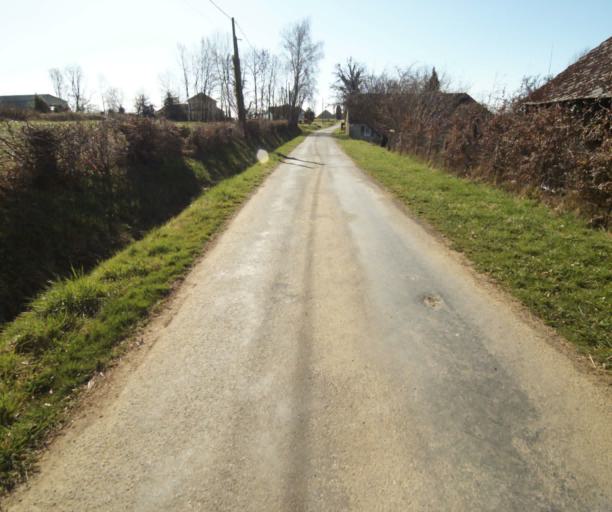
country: FR
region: Limousin
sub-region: Departement de la Correze
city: Seilhac
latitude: 45.3903
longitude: 1.7539
